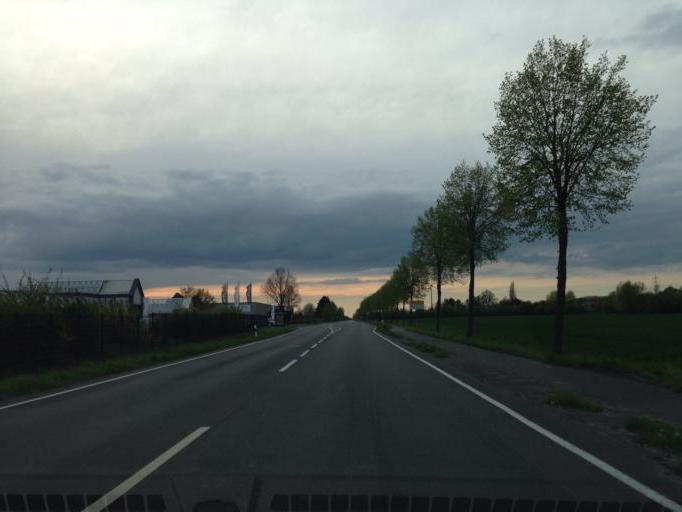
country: DE
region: North Rhine-Westphalia
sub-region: Regierungsbezirk Munster
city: Muenster
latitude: 52.0016
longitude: 7.5515
